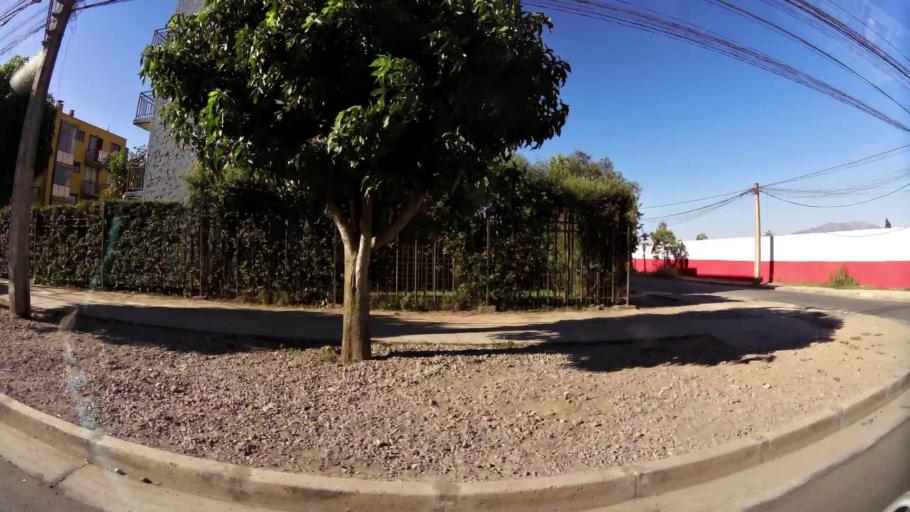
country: CL
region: O'Higgins
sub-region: Provincia de Colchagua
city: Chimbarongo
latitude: -34.5937
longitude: -70.9952
